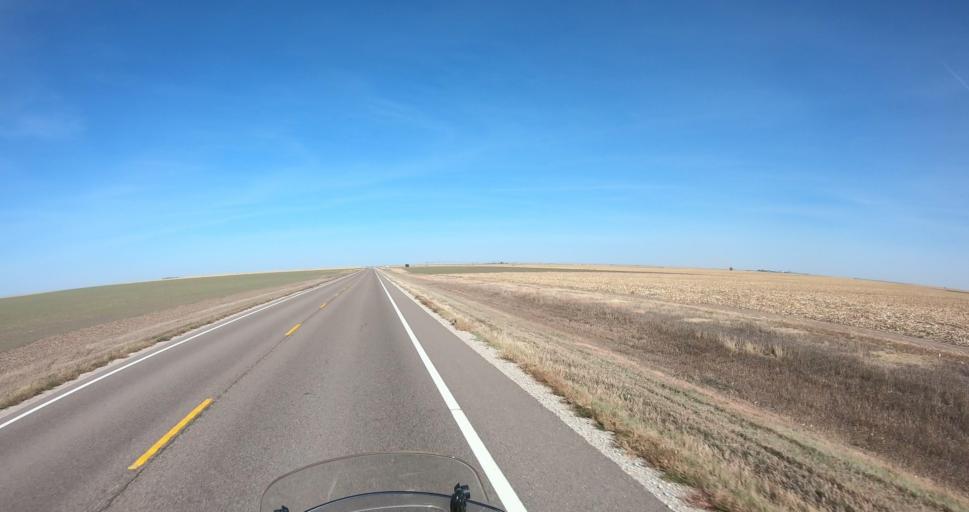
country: US
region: Kansas
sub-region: Thomas County
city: Colby
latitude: 39.4132
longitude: -100.8710
